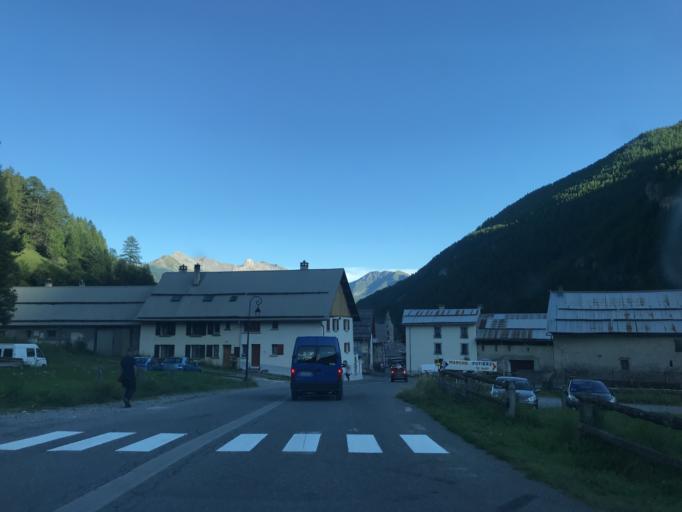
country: FR
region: Provence-Alpes-Cote d'Azur
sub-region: Departement des Hautes-Alpes
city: Guillestre
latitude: 44.7686
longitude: 6.7376
